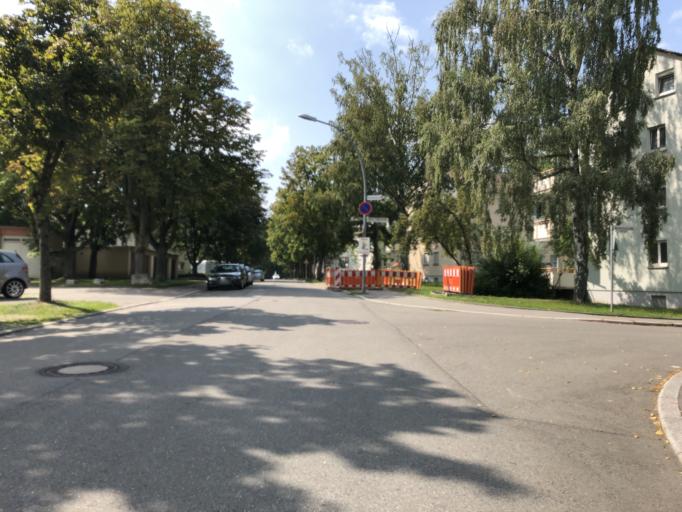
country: DE
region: Baden-Wuerttemberg
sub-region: Regierungsbezirk Stuttgart
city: Sindelfingen
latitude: 48.7271
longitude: 9.0071
